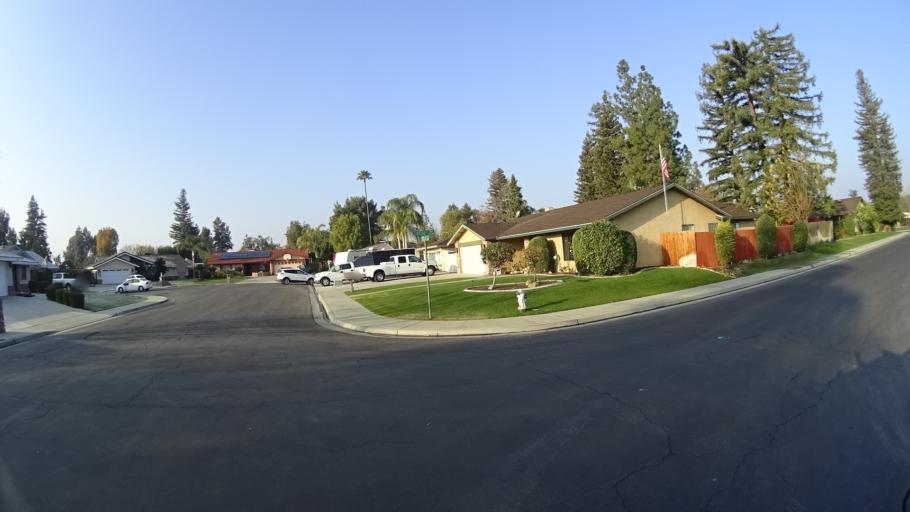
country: US
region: California
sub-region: Kern County
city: Greenacres
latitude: 35.3230
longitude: -119.0783
